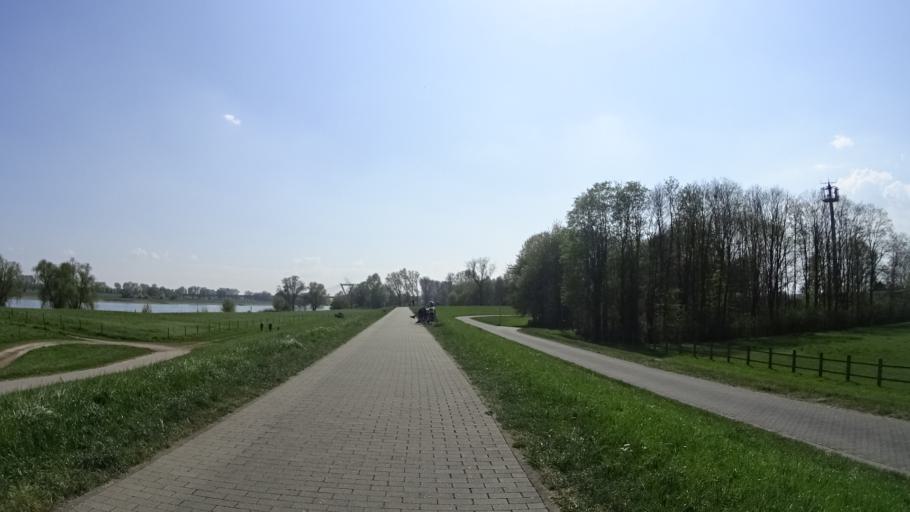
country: DE
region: North Rhine-Westphalia
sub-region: Regierungsbezirk Dusseldorf
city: Meerbusch
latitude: 51.2901
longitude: 6.7112
